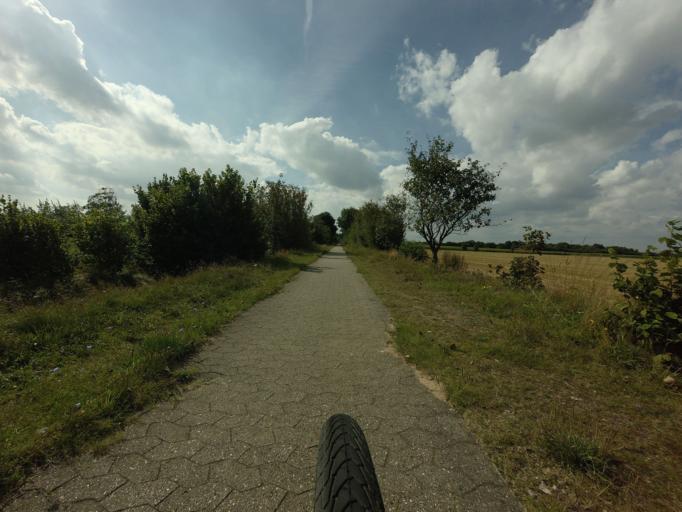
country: DK
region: Central Jutland
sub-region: Viborg Kommune
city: Karup
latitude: 56.3340
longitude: 9.2389
